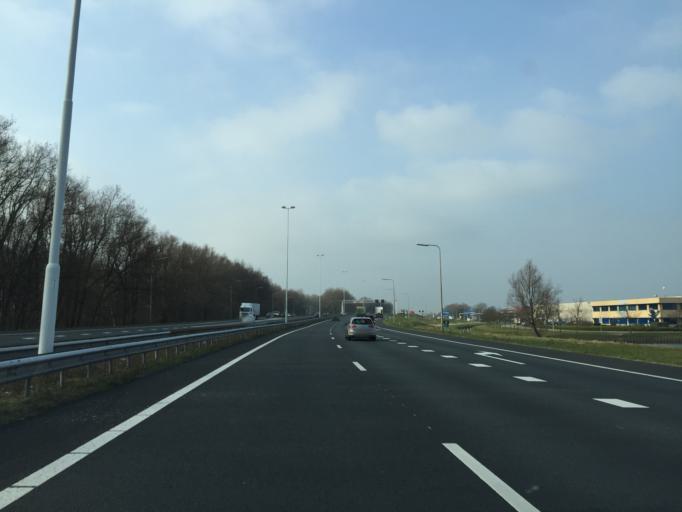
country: NL
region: South Holland
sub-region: Gemeente Westland
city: Maasdijk
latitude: 51.9484
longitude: 4.2345
